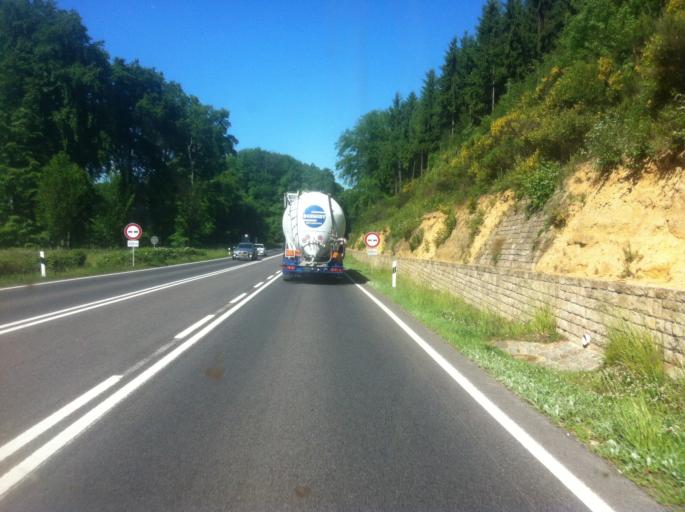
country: LU
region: Grevenmacher
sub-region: Canton d'Echternach
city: Consdorf
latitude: 49.7452
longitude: 6.3029
